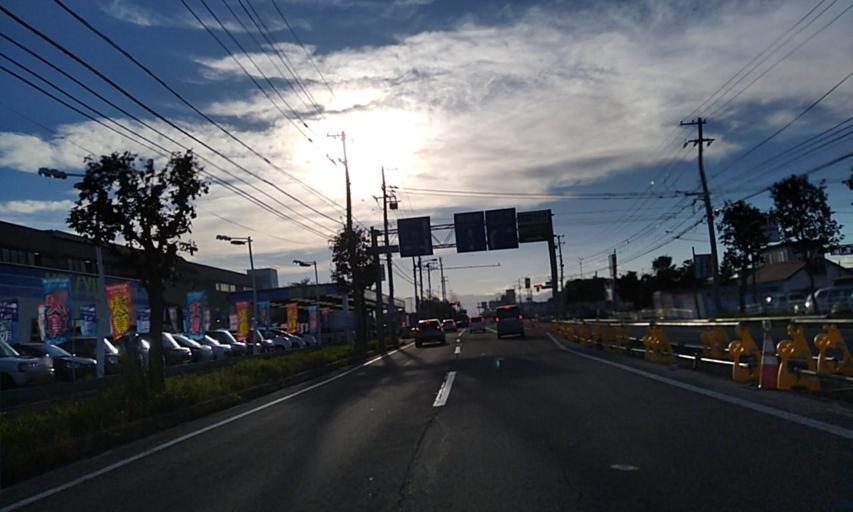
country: JP
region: Hokkaido
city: Obihiro
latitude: 42.9293
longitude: 143.1657
